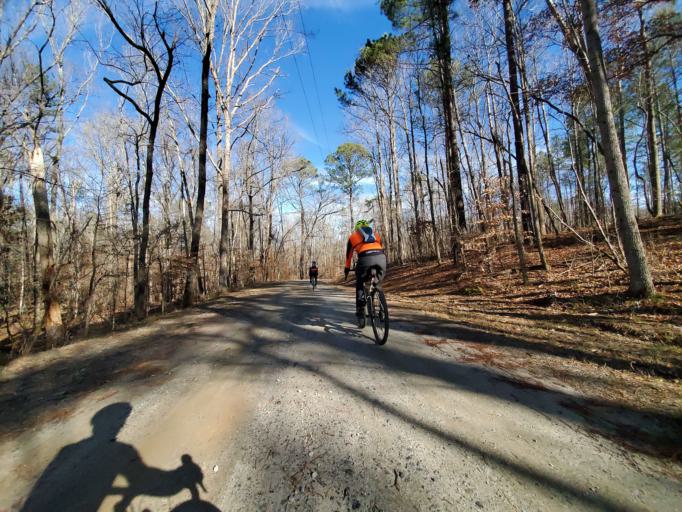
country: US
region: Georgia
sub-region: Fulton County
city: Chattahoochee Hills
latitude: 33.5678
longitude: -84.8082
